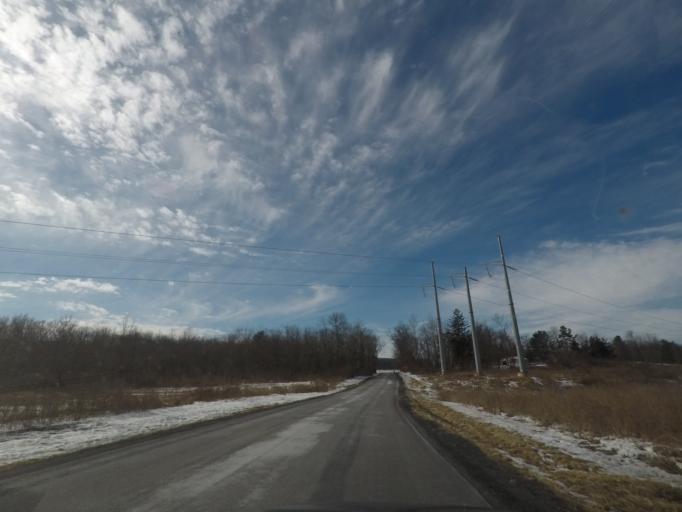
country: US
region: New York
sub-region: Albany County
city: Voorheesville
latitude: 42.6589
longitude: -73.9616
